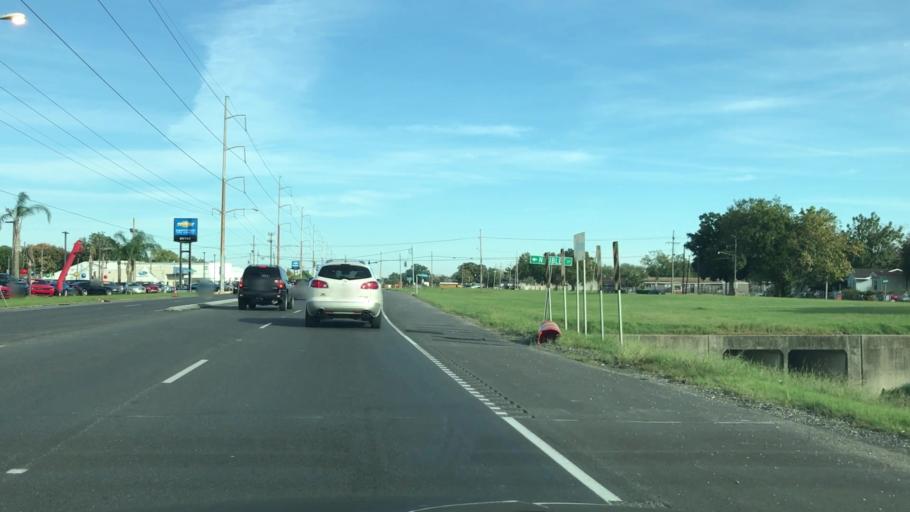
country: US
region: Louisiana
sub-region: Jefferson Parish
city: Kenner
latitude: 29.9792
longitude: -90.2339
